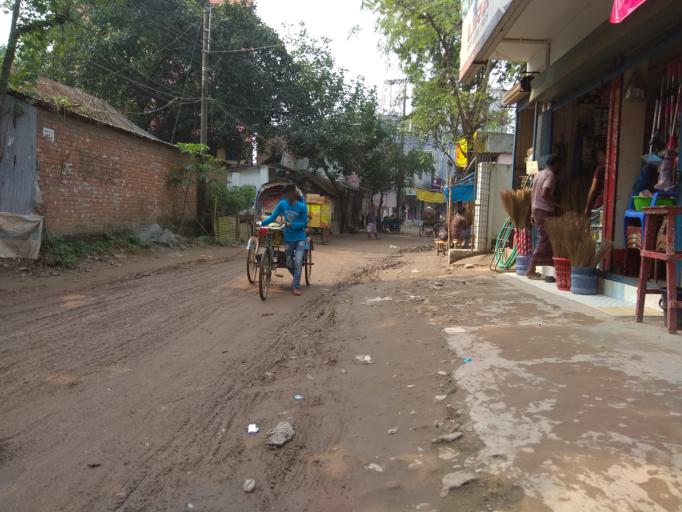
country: BD
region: Dhaka
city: Tungi
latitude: 23.8543
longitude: 90.3836
